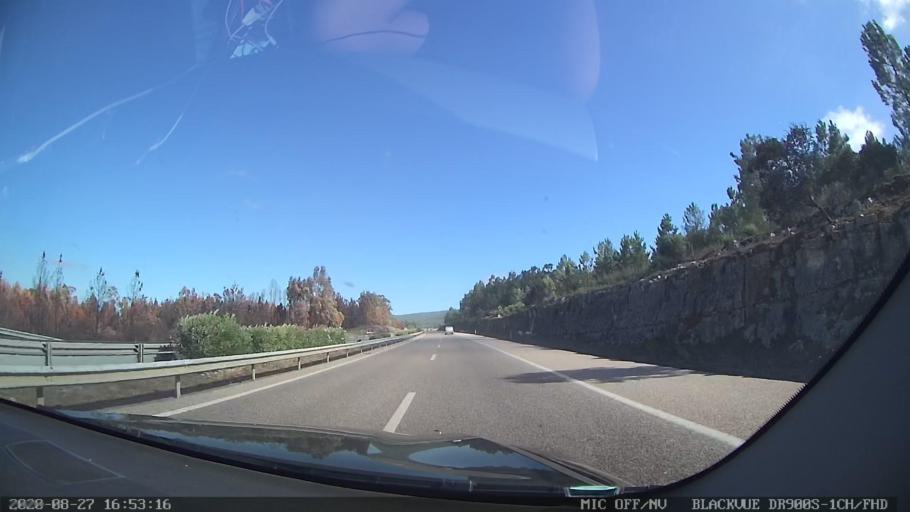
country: PT
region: Santarem
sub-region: Ourem
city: Fatima
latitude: 39.5828
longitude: -8.6600
